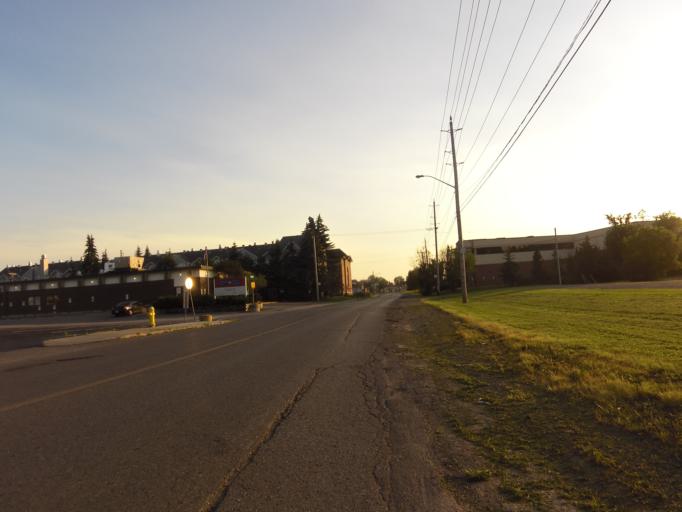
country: CA
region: Ontario
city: Bells Corners
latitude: 45.3297
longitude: -75.8142
